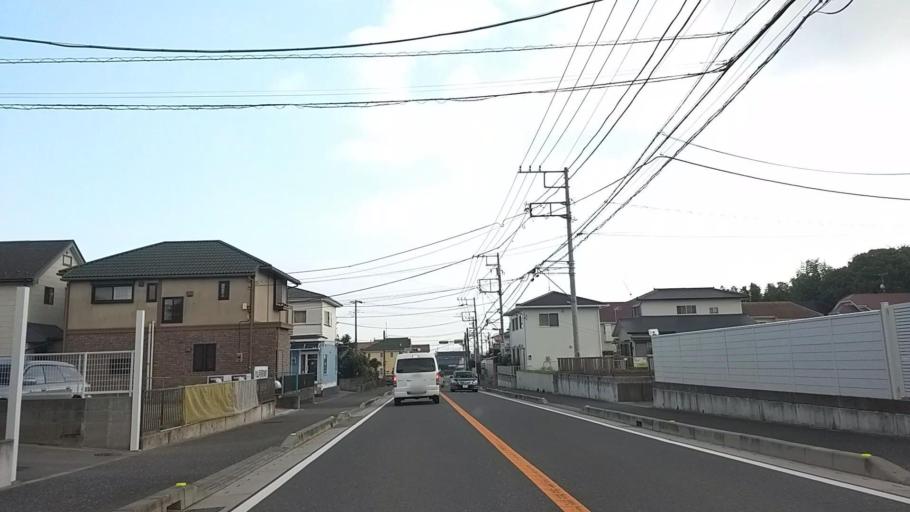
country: JP
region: Kanagawa
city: Isehara
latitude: 35.3797
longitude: 139.3004
